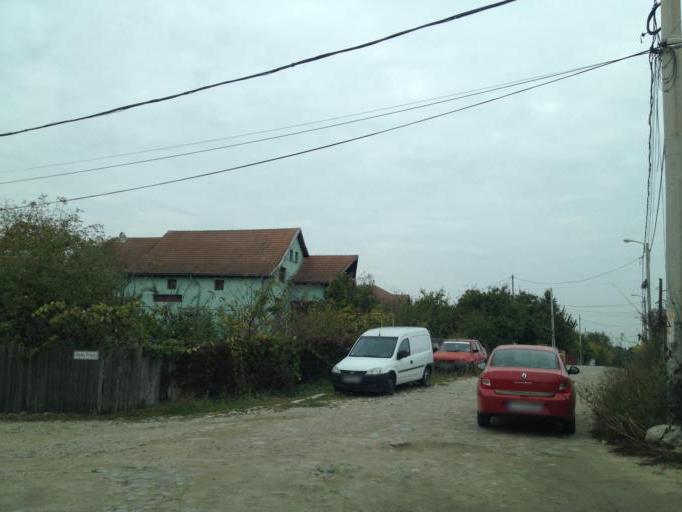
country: RO
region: Dolj
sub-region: Municipiul Craiova
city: Facai
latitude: 44.2928
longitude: 23.8073
